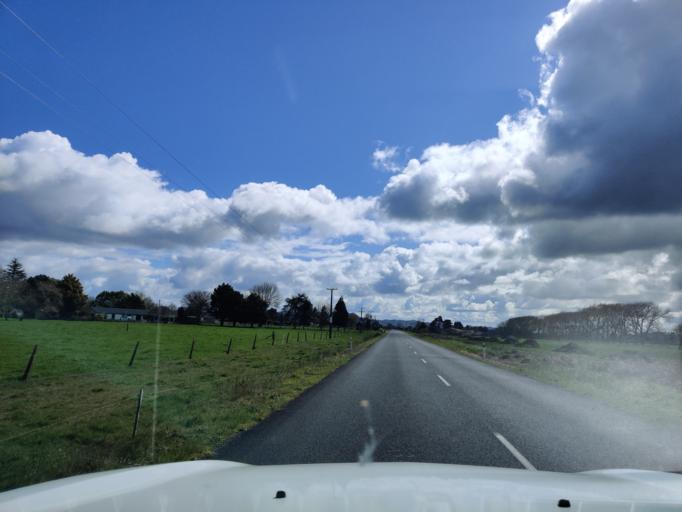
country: NZ
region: Waikato
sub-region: Waikato District
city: Ngaruawahia
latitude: -37.5960
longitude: 175.2957
